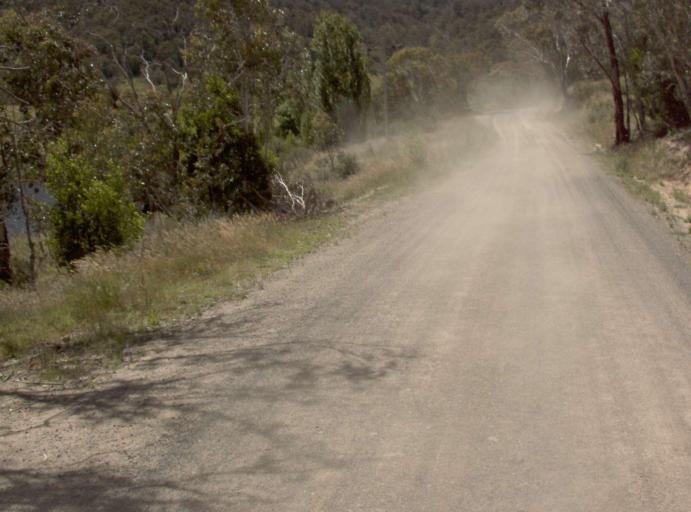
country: AU
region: New South Wales
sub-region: Bombala
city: Bombala
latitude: -37.1399
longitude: 148.6632
